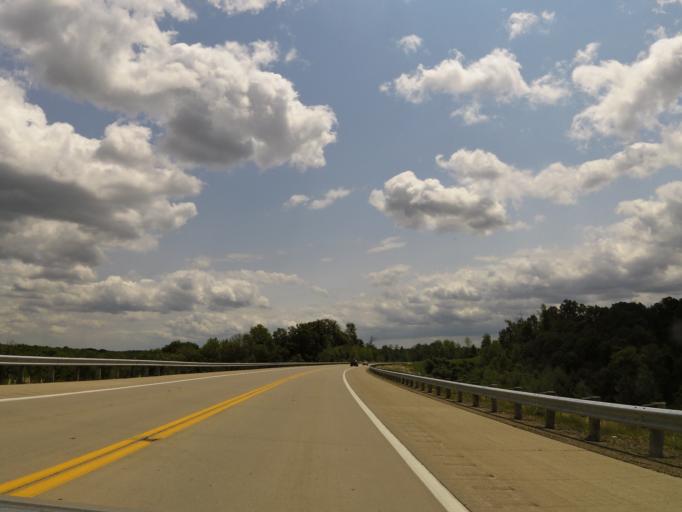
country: US
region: Ohio
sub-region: Athens County
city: Athens
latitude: 39.2714
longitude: -82.0886
